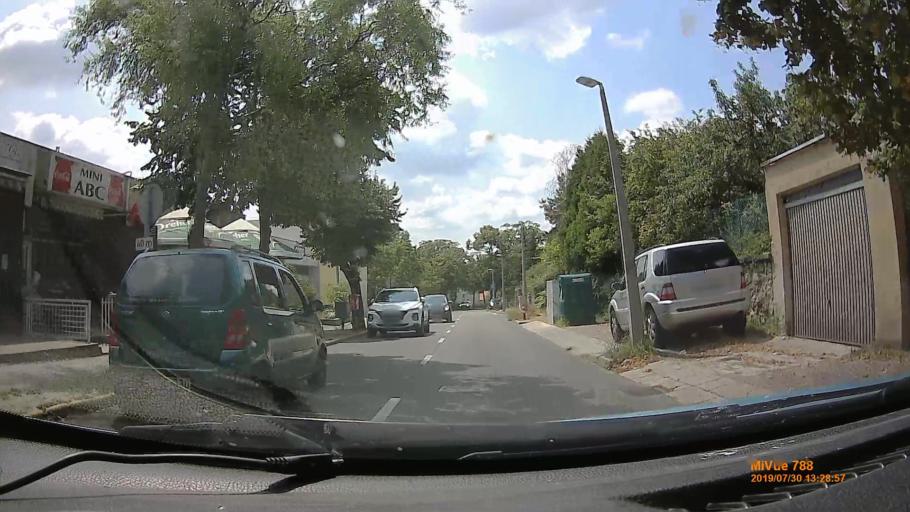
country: HU
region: Baranya
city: Pecs
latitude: 46.0840
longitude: 18.2235
